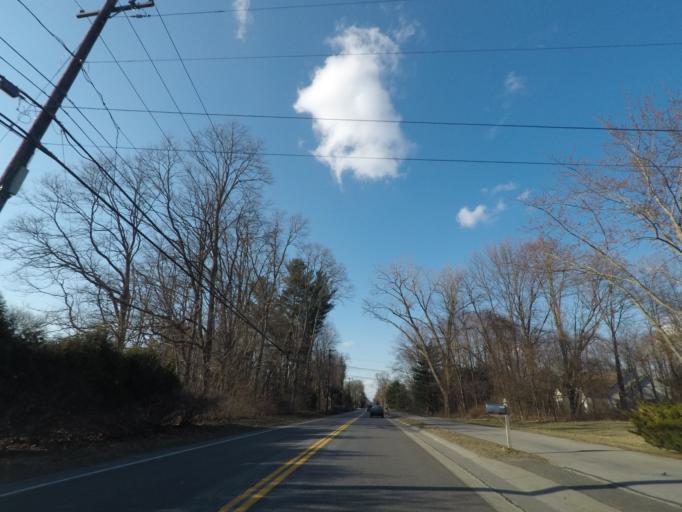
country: US
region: New York
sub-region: Saratoga County
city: Country Knolls
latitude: 42.8449
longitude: -73.7942
